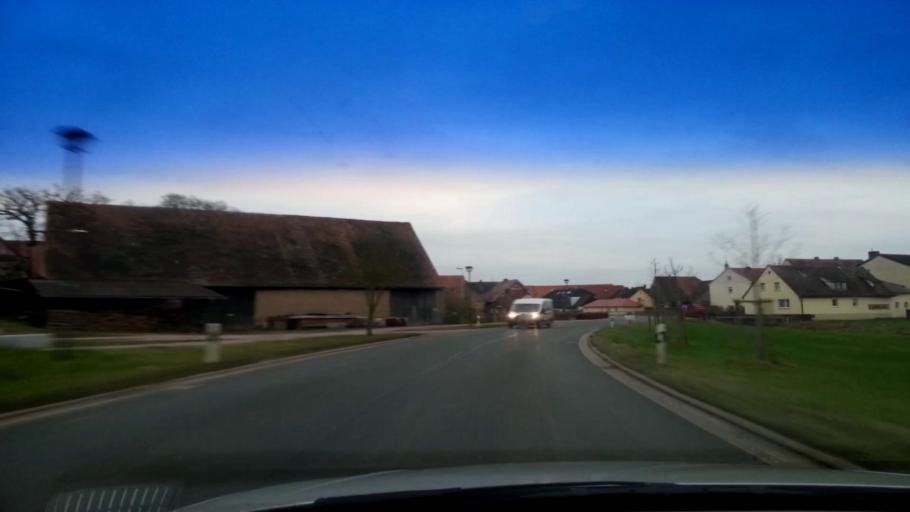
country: DE
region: Bavaria
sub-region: Upper Franconia
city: Pommersfelden
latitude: 49.7750
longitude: 10.8019
